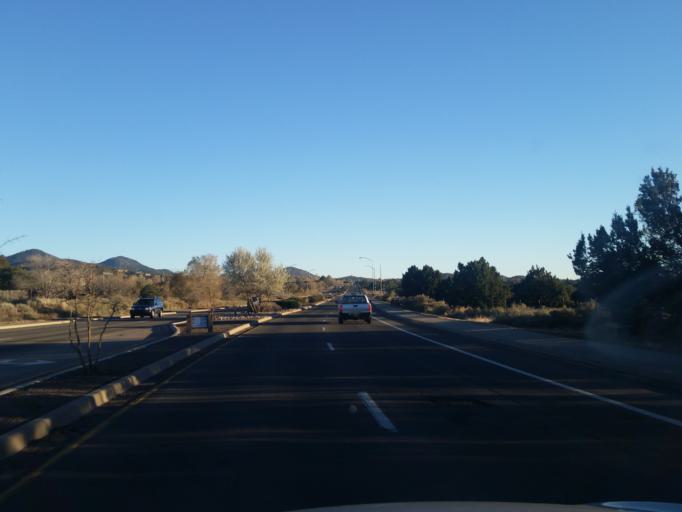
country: US
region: New Mexico
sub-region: Santa Fe County
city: Santa Fe
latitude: 35.6536
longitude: -105.9379
